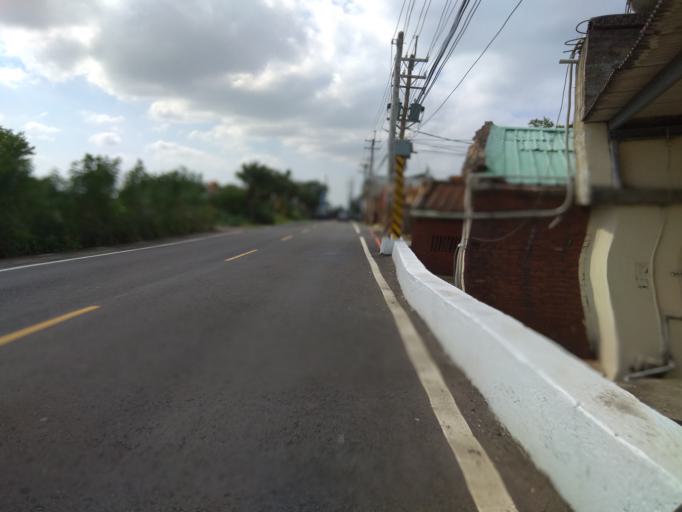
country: TW
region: Taiwan
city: Taoyuan City
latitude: 25.0624
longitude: 121.2364
